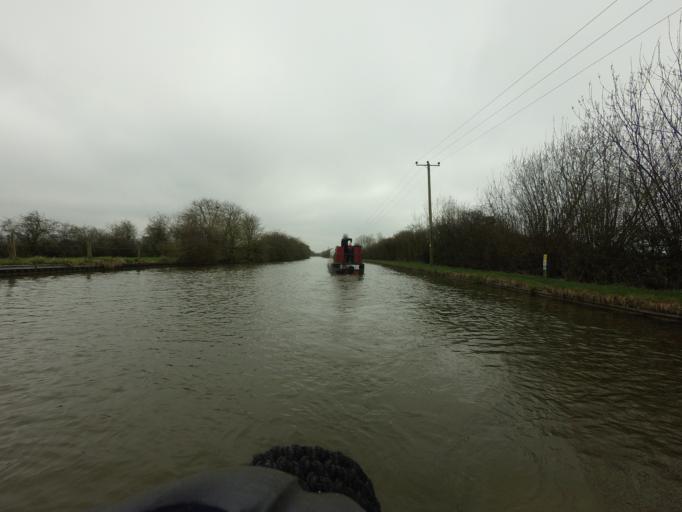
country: GB
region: England
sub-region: Buckinghamshire
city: Cheddington
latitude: 51.8645
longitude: -0.6481
